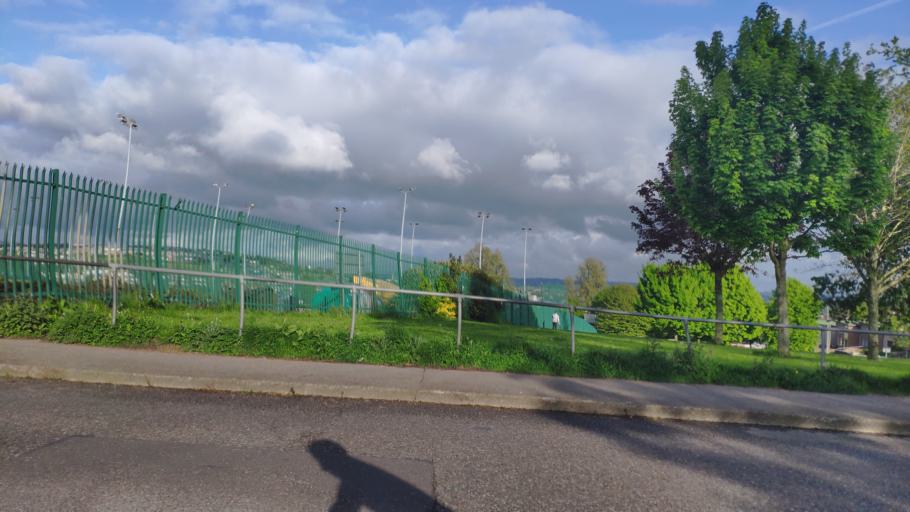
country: IE
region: Munster
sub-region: County Cork
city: Cork
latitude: 51.9069
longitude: -8.4905
